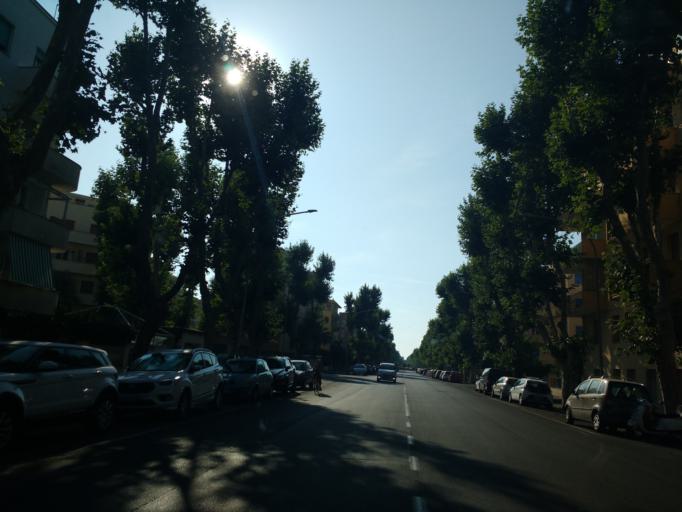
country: IT
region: Latium
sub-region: Citta metropolitana di Roma Capitale
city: Lido di Ostia
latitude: 41.7264
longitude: 12.2900
